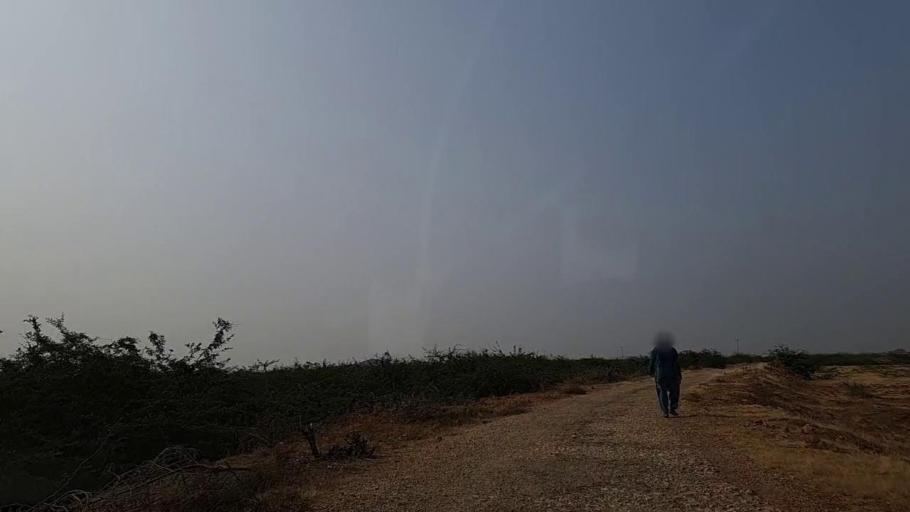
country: PK
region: Sindh
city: Thatta
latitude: 24.7217
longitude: 67.8316
